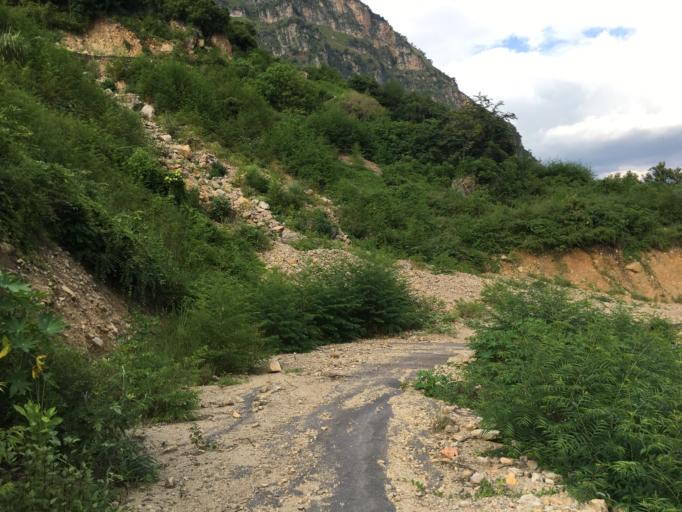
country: CN
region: Guizhou Sheng
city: Anshun
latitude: 25.7780
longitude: 105.3901
